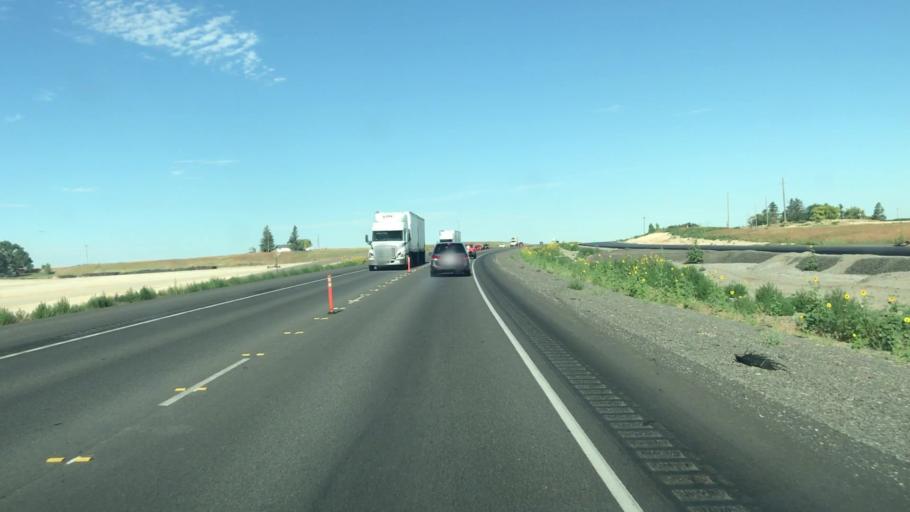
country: US
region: Idaho
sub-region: Twin Falls County
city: Hansen
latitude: 42.5753
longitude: -114.1033
